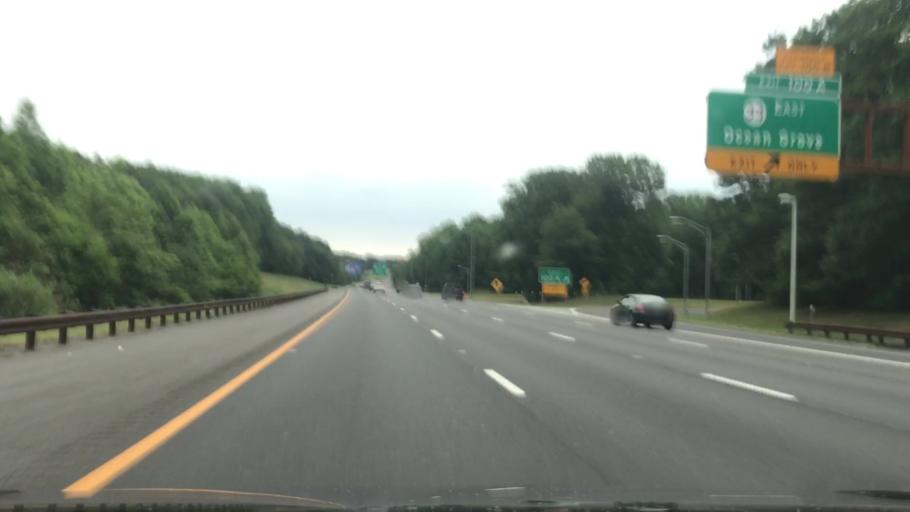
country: US
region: New Jersey
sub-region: Monmouth County
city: Shark River Hills
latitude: 40.2137
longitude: -74.0990
